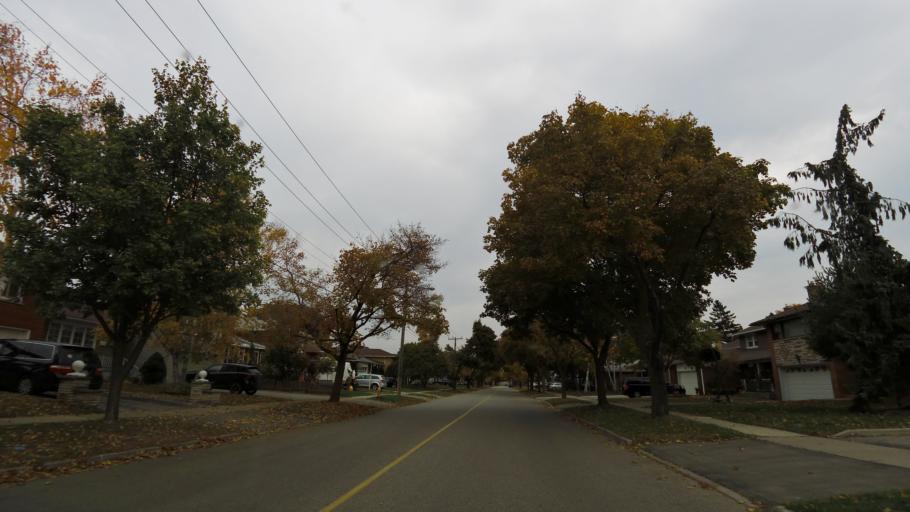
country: CA
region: Ontario
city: Etobicoke
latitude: 43.6835
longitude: -79.5393
